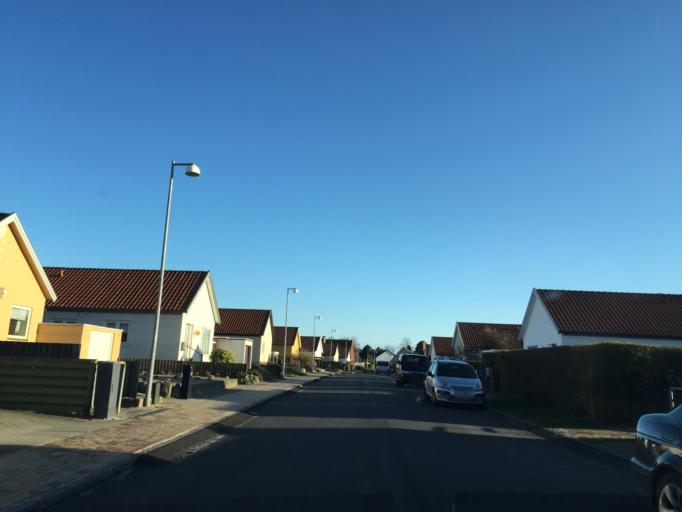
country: DK
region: South Denmark
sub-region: Odense Kommune
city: Odense
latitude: 55.3778
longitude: 10.3936
